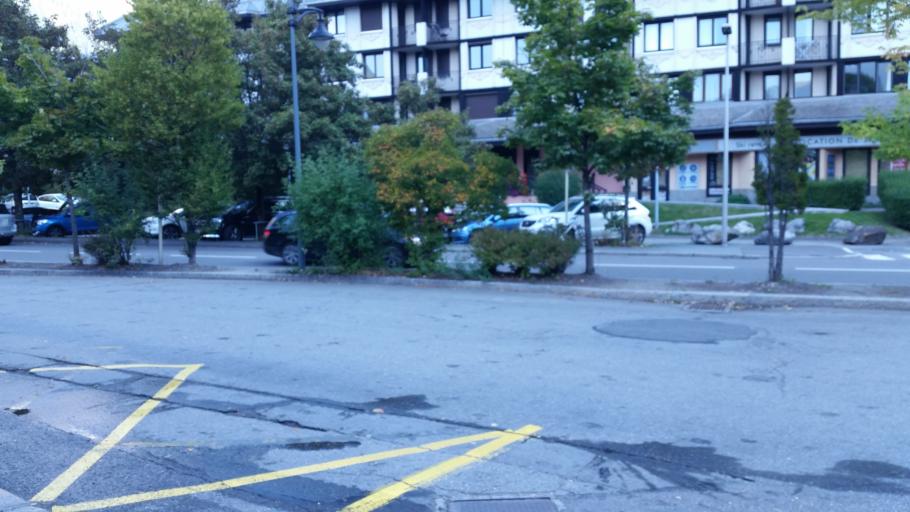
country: FR
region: Rhone-Alpes
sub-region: Departement de la Haute-Savoie
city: Chamonix-Mont-Blanc
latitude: 45.9173
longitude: 6.8674
